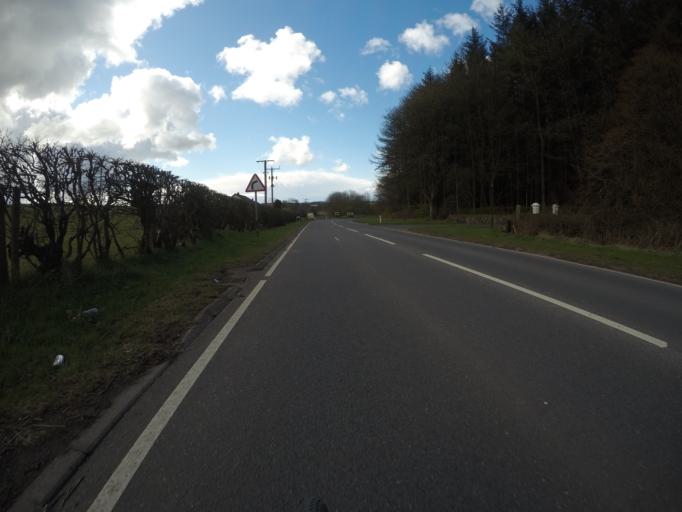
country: GB
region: Scotland
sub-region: North Ayrshire
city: Dalry
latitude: 55.7124
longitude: -4.7008
